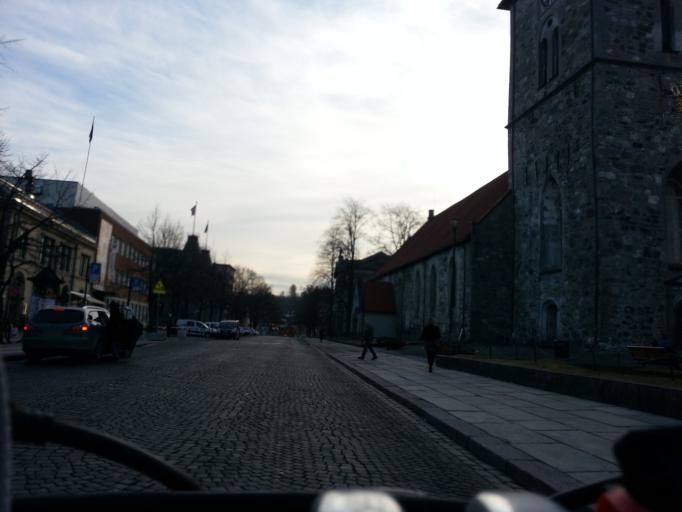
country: NO
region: Sor-Trondelag
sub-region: Trondheim
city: Trondheim
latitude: 63.4304
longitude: 10.3970
